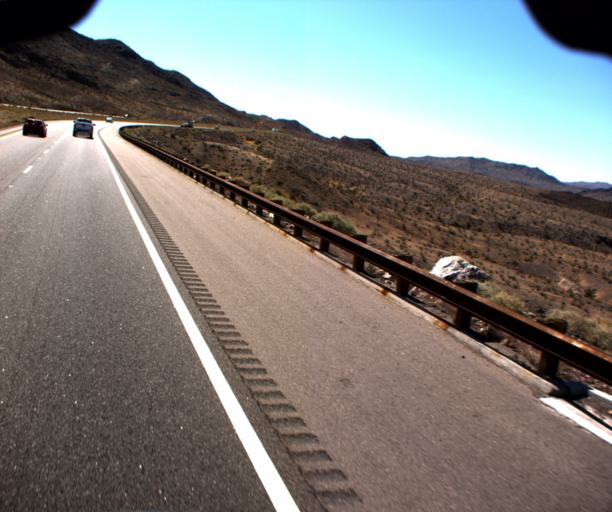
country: US
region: Nevada
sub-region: Clark County
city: Boulder City
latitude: 35.8587
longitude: -114.5978
